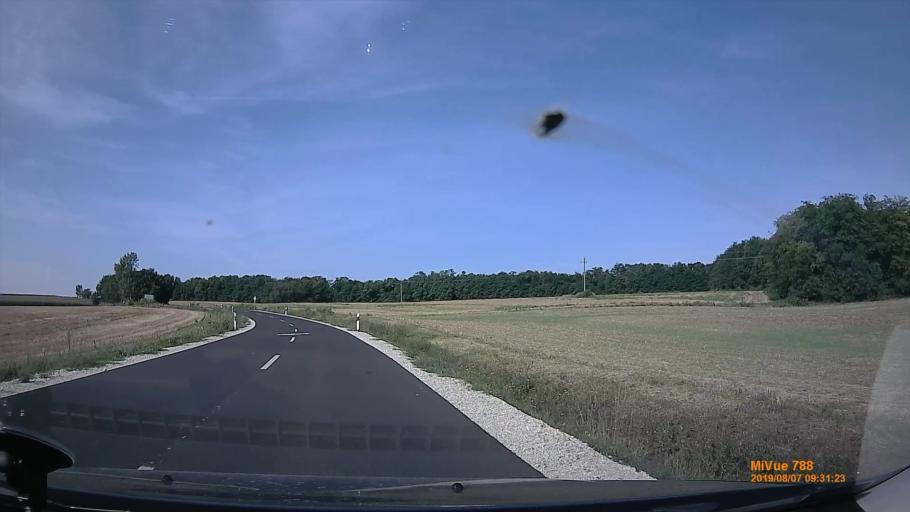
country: HU
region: Zala
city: Sarmellek
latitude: 46.7433
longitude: 17.1734
